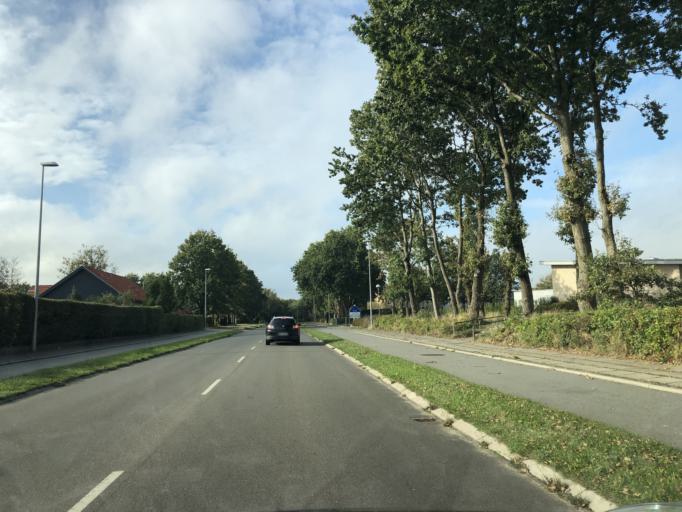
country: DK
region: Central Jutland
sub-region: Holstebro Kommune
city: Holstebro
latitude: 56.3668
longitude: 8.5968
